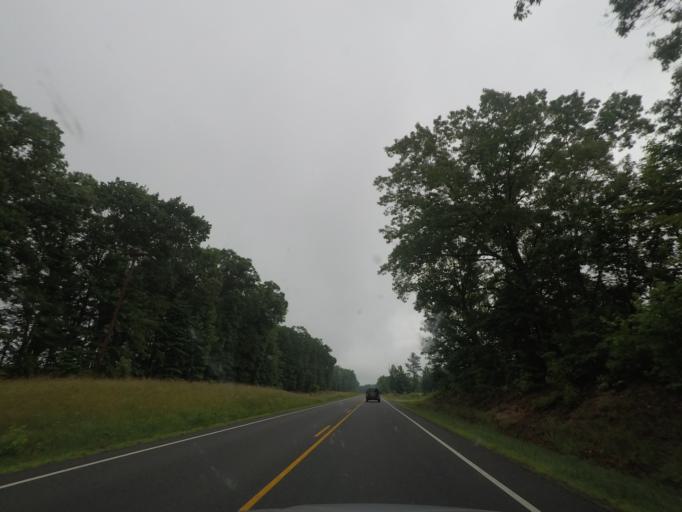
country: US
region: Virginia
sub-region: Prince Edward County
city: Hampden Sydney
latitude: 37.1053
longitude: -78.4694
